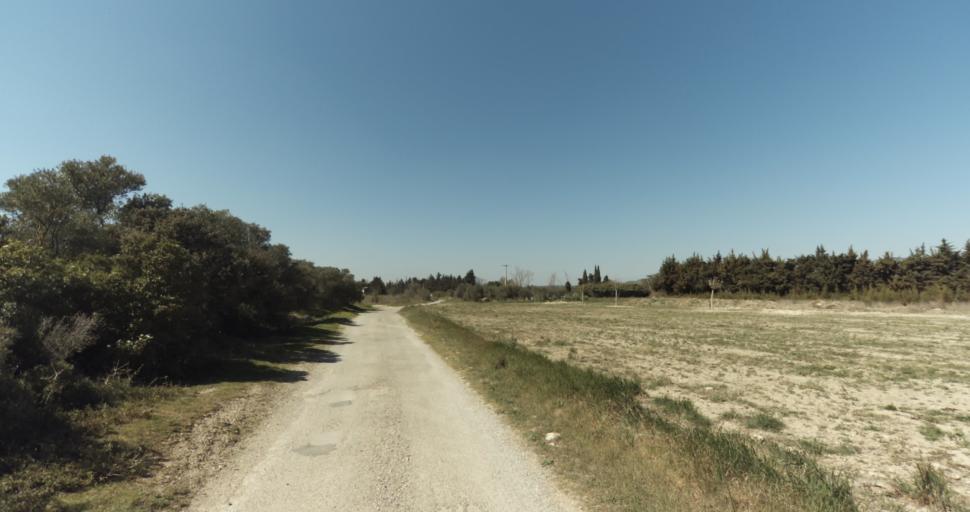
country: FR
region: Provence-Alpes-Cote d'Azur
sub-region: Departement des Bouches-du-Rhone
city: Pelissanne
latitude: 43.6229
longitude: 5.1630
